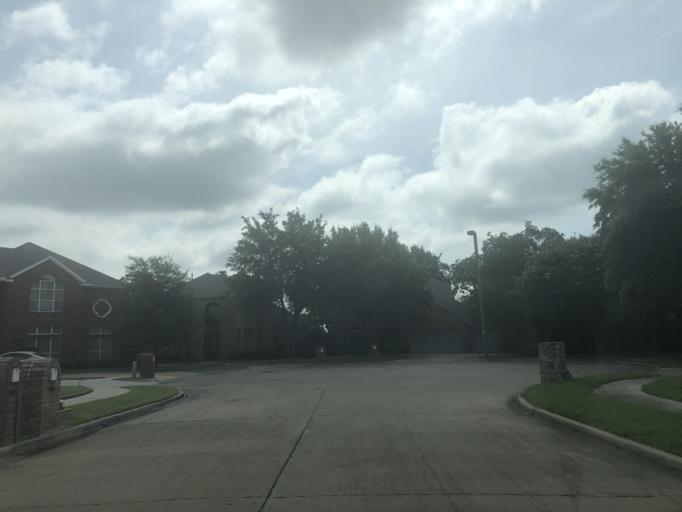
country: US
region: Texas
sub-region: Dallas County
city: Irving
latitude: 32.8023
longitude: -96.9678
